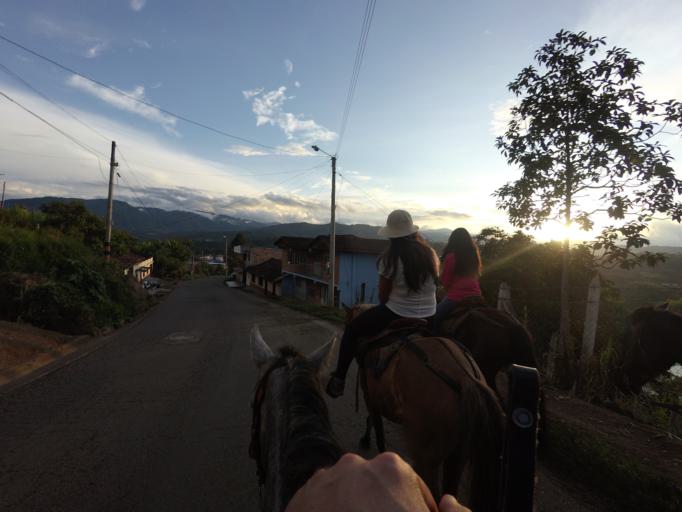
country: CO
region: Huila
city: San Agustin
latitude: 1.8880
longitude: -76.2723
